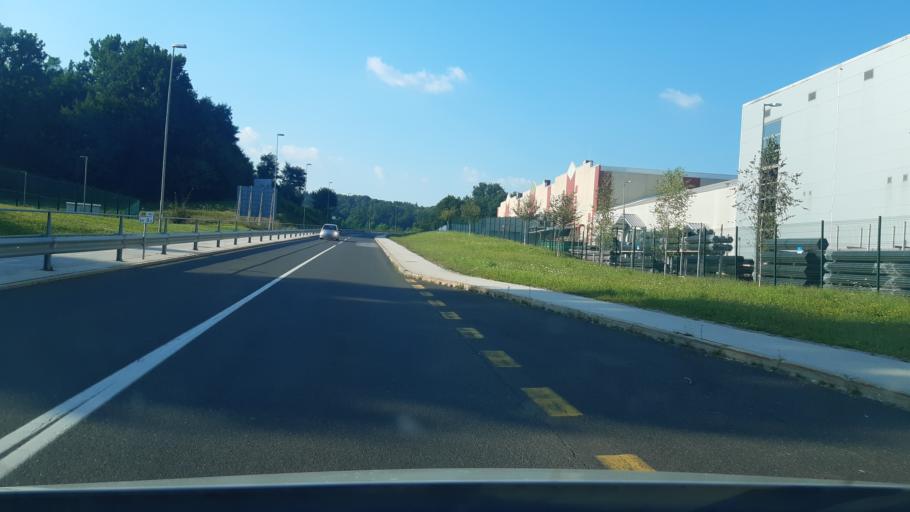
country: SI
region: Crnomelj
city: Crnomelj
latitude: 45.5728
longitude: 15.1806
